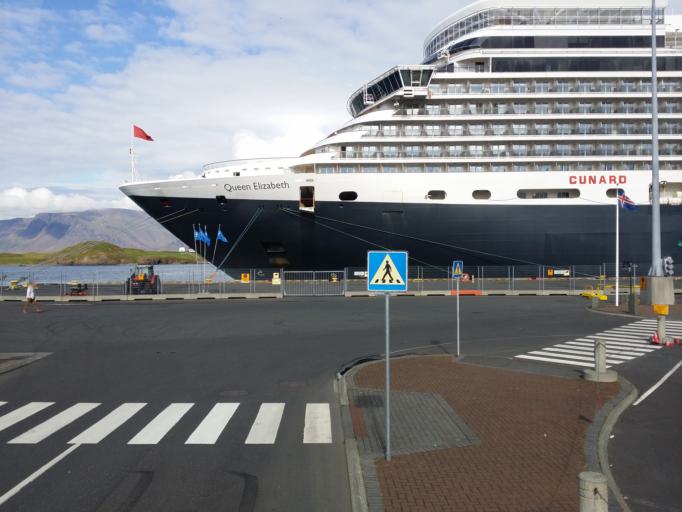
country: IS
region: Capital Region
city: Reykjavik
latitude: 64.1559
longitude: -21.8657
